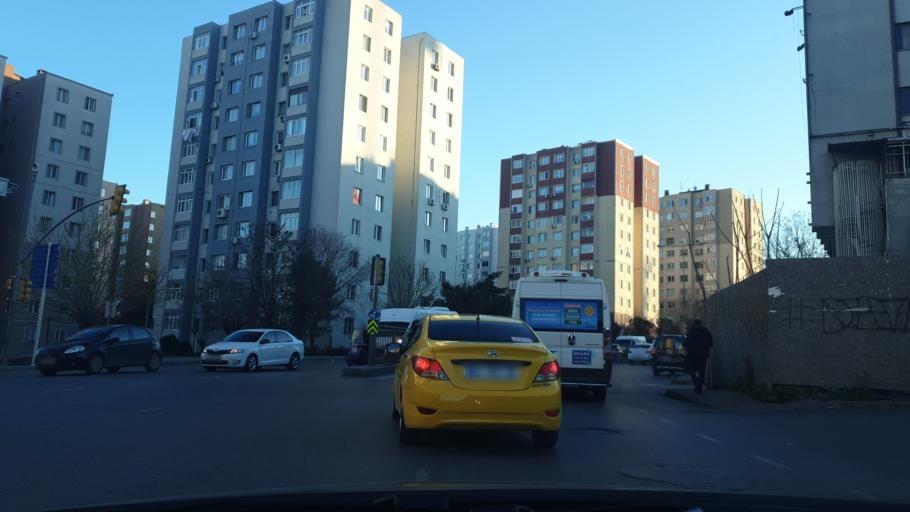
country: TR
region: Istanbul
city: merter keresteciler
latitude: 41.0088
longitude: 28.8751
